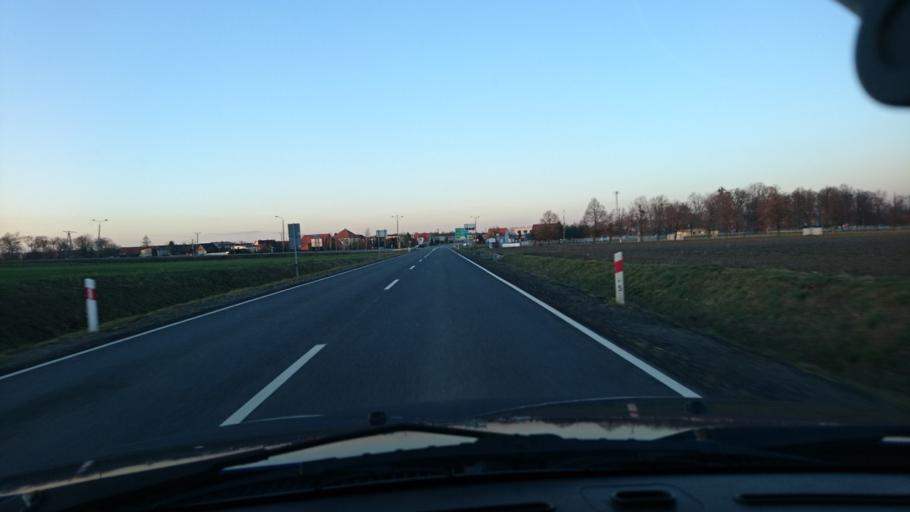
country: PL
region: Silesian Voivodeship
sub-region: Powiat gliwicki
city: Wielowies
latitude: 50.5020
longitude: 18.6052
